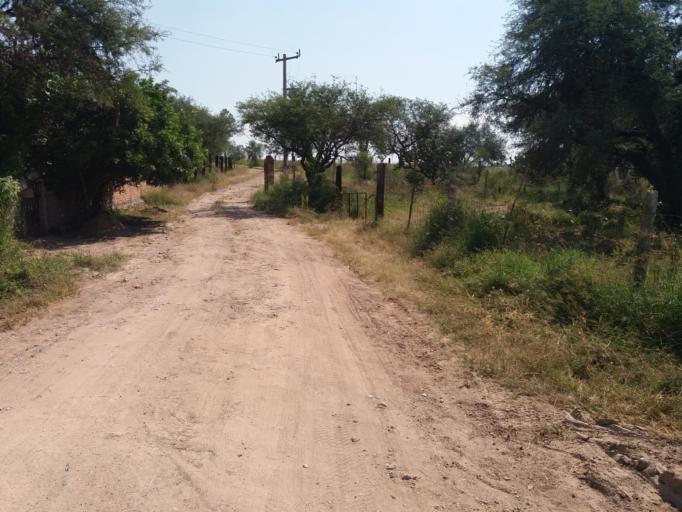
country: MX
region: Aguascalientes
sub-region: Aguascalientes
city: Penuelas (El Cienegal)
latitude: 21.7583
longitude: -102.2667
